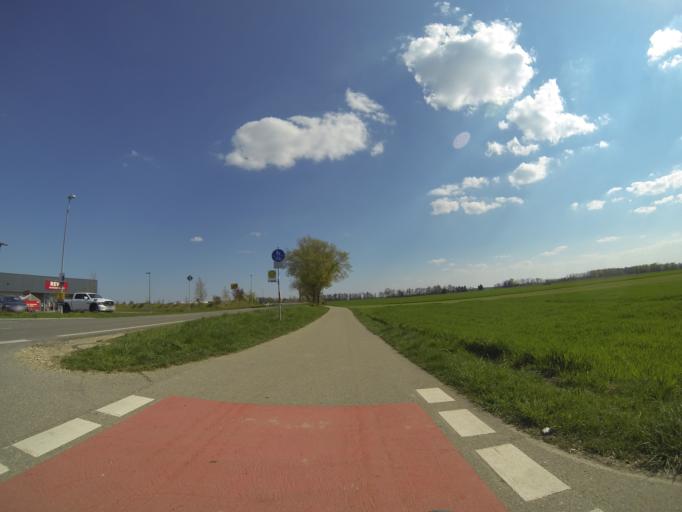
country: DE
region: Baden-Wuerttemberg
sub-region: Tuebingen Region
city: Laupheim
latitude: 48.2230
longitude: 9.8931
